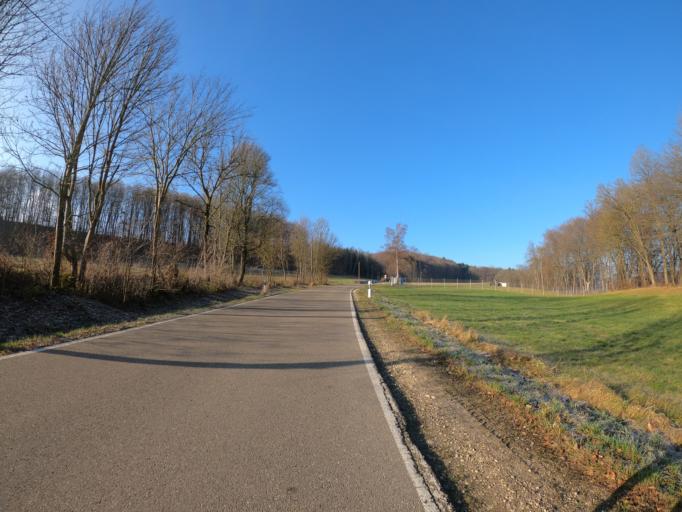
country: DE
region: Baden-Wuerttemberg
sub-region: Tuebingen Region
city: Amstetten
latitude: 48.5883
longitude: 9.8619
